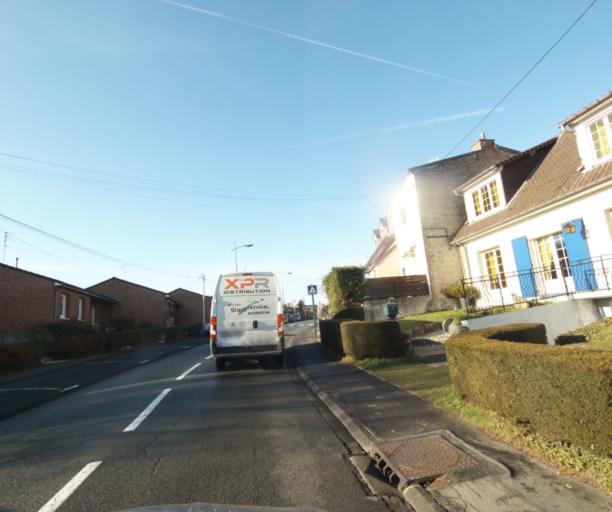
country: FR
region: Nord-Pas-de-Calais
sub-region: Departement du Nord
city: Aulnoy-lez-Valenciennes
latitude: 50.3329
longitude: 3.5275
